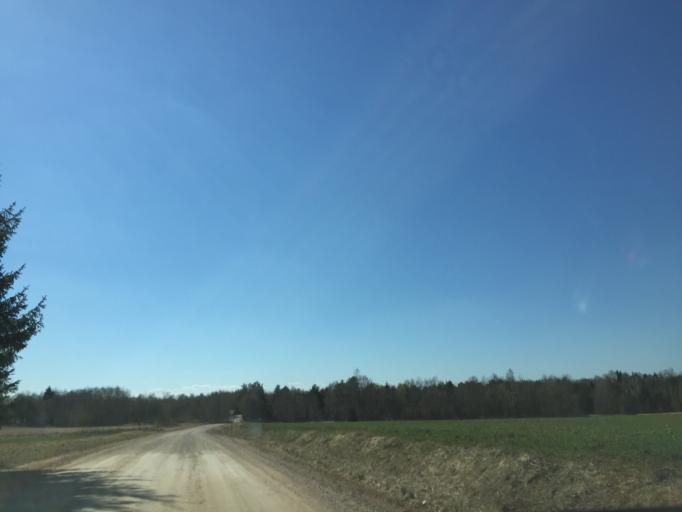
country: EE
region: Viljandimaa
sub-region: Viiratsi vald
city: Viiratsi
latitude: 58.3148
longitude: 25.6890
